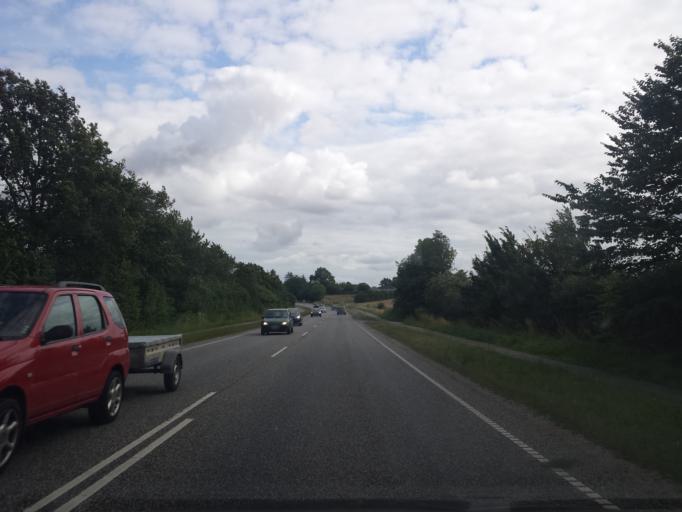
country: DK
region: South Denmark
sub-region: Sonderborg Kommune
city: Guderup
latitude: 54.9921
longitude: 9.8583
